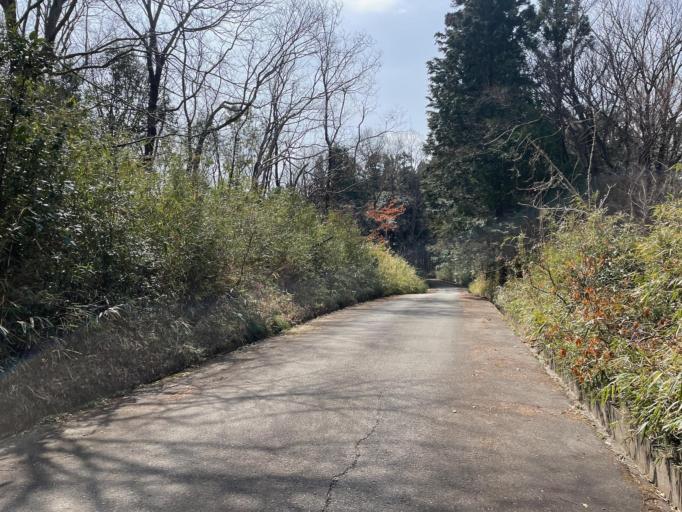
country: JP
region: Saitama
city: Ogawa
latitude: 36.0825
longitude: 139.2842
